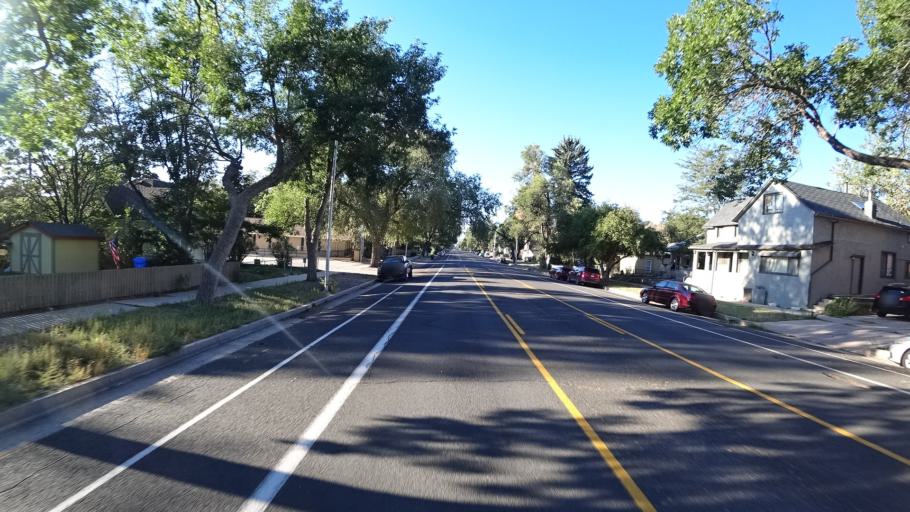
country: US
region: Colorado
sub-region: El Paso County
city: Colorado Springs
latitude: 38.8432
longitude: -104.8324
